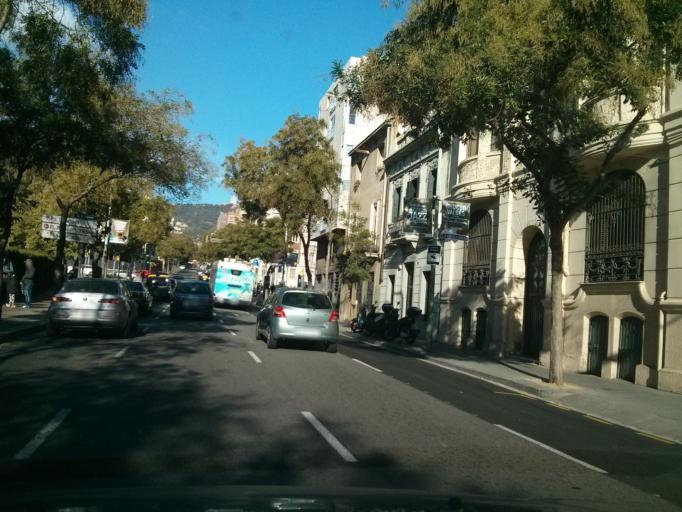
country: ES
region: Catalonia
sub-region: Provincia de Barcelona
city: Sarria-Sant Gervasi
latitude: 41.3986
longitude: 2.1347
